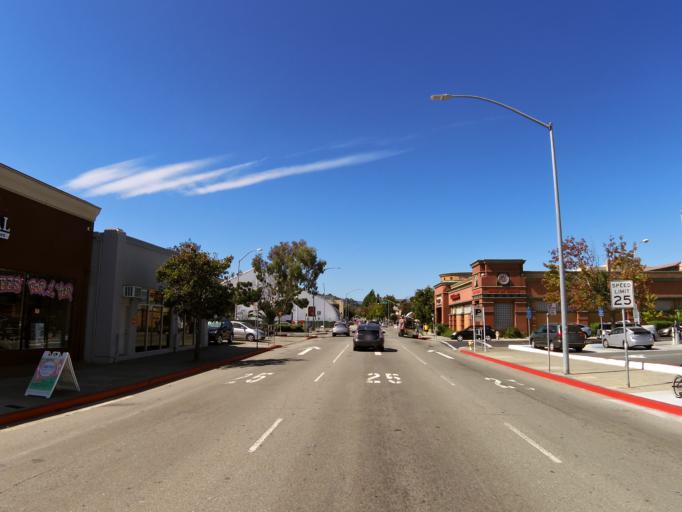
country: US
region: California
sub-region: Marin County
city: San Rafael
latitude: 37.9717
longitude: -122.5246
